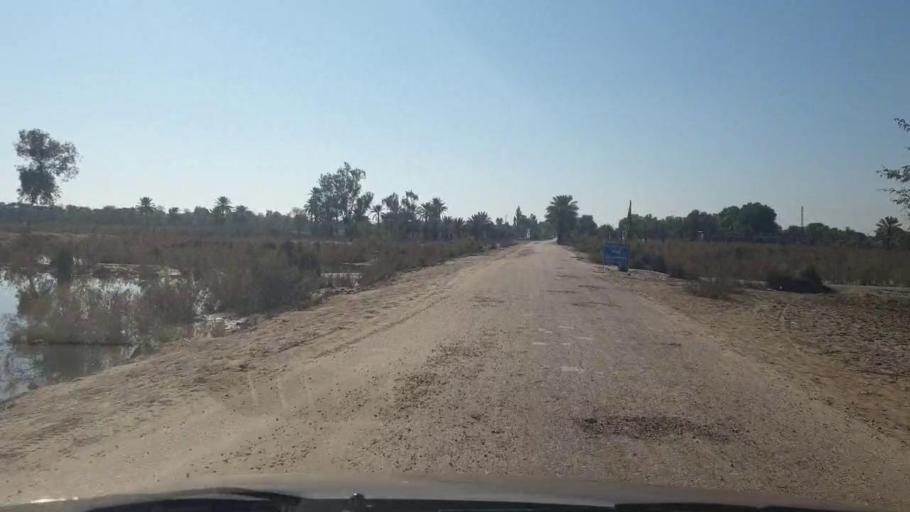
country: PK
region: Sindh
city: Bozdar
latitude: 27.1280
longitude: 68.6342
